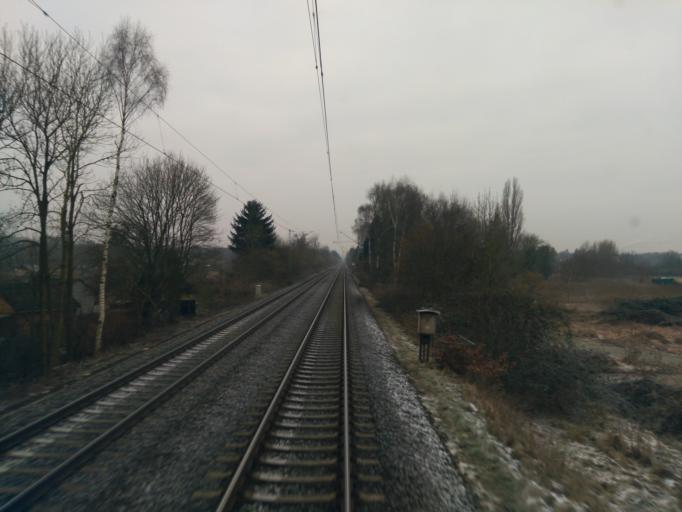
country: DE
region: Bremen
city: Bremen
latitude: 53.1004
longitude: 8.8505
